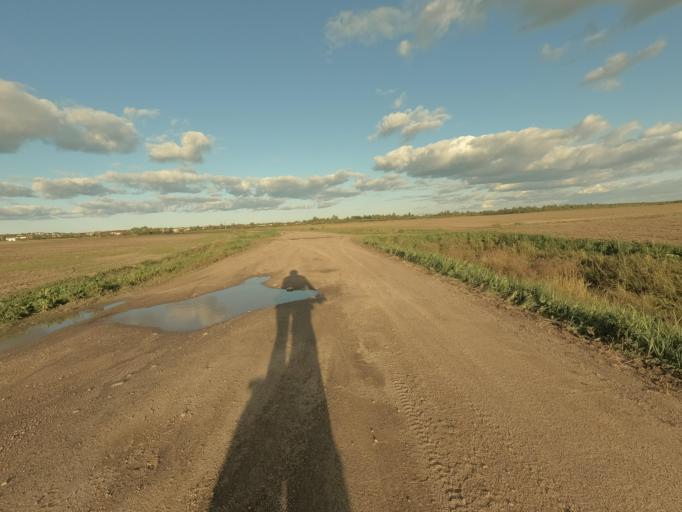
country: RU
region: Leningrad
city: Otradnoye
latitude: 59.8641
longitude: 30.7567
